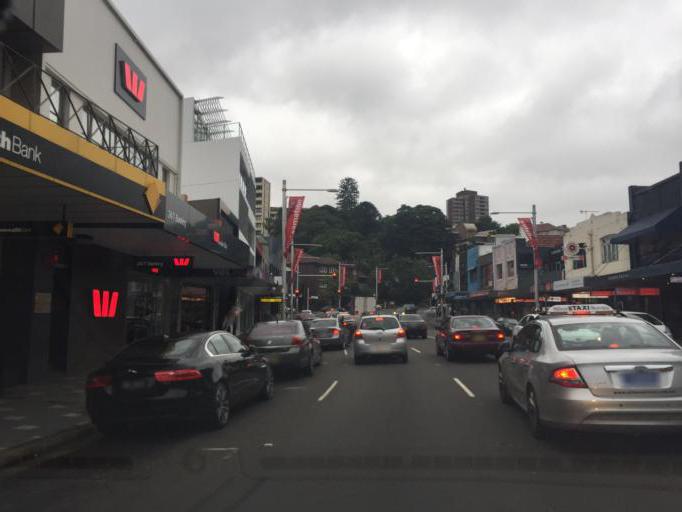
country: AU
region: New South Wales
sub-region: Woollahra
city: Bellevue Hill
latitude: -33.8778
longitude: 151.2429
